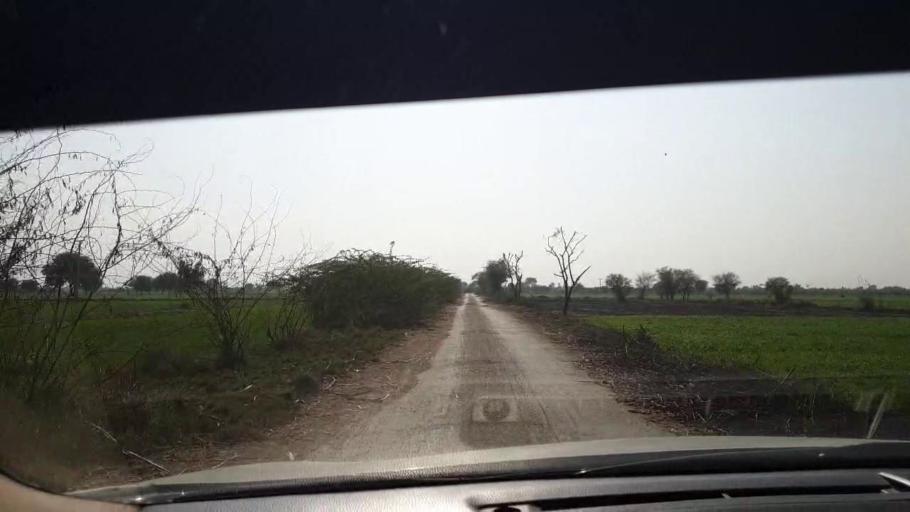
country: PK
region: Sindh
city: Berani
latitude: 25.8459
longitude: 68.7254
